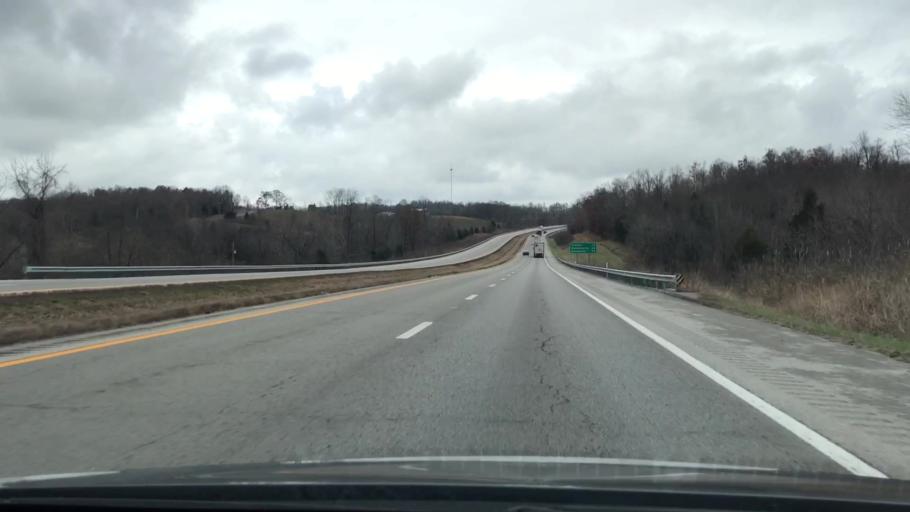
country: US
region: Kentucky
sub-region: Christian County
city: Hopkinsville
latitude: 36.9111
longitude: -87.4741
